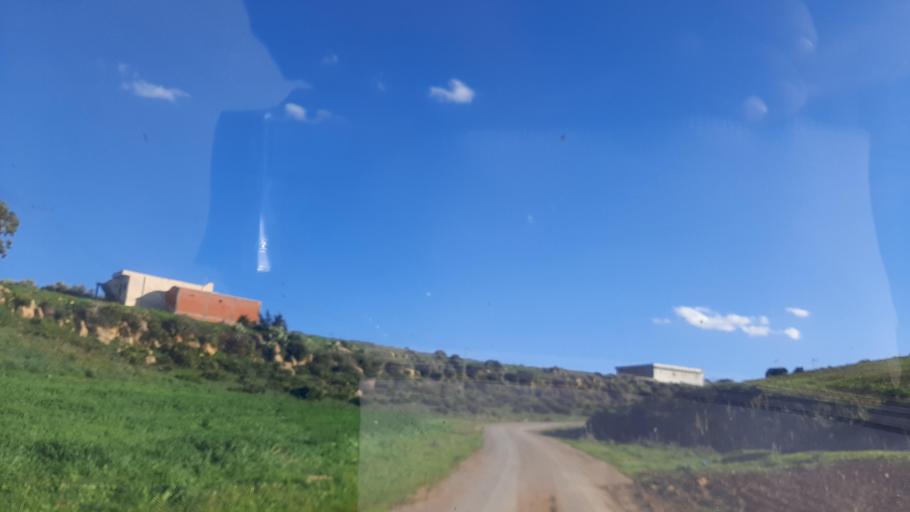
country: TN
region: Nabul
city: El Mida
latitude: 36.8105
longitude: 10.8450
